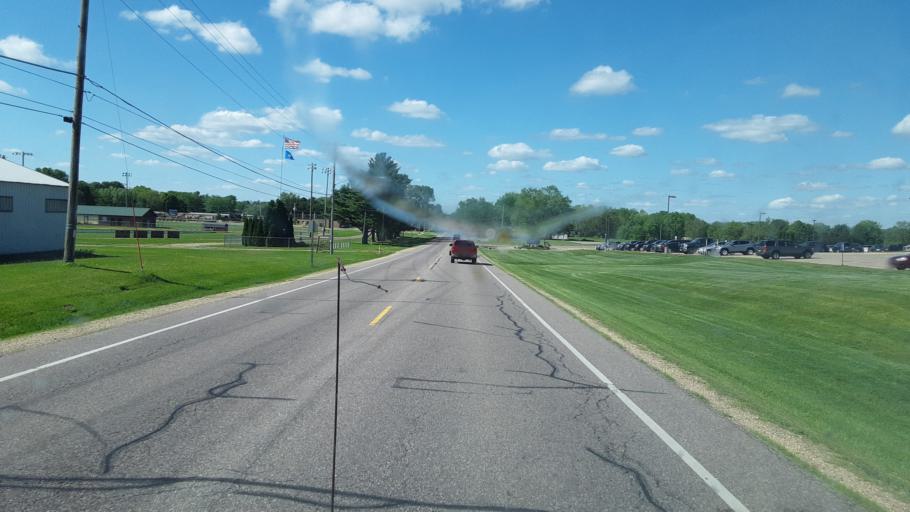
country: US
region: Wisconsin
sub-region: Juneau County
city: Mauston
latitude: 43.7823
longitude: -90.0768
